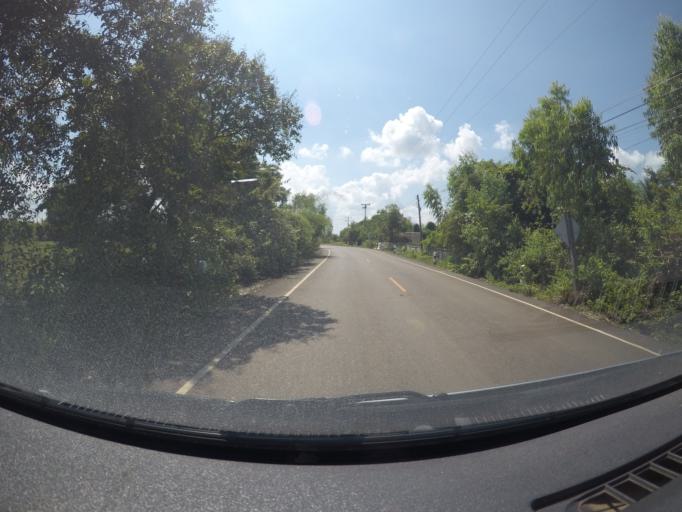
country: TH
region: Sakon Nakhon
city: Sakon Nakhon
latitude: 17.2159
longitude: 104.1344
